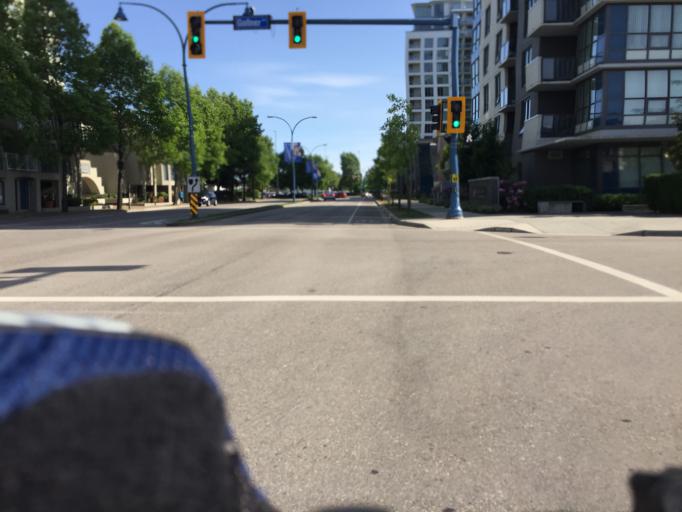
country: CA
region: British Columbia
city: Richmond
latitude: 49.1689
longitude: -123.1403
